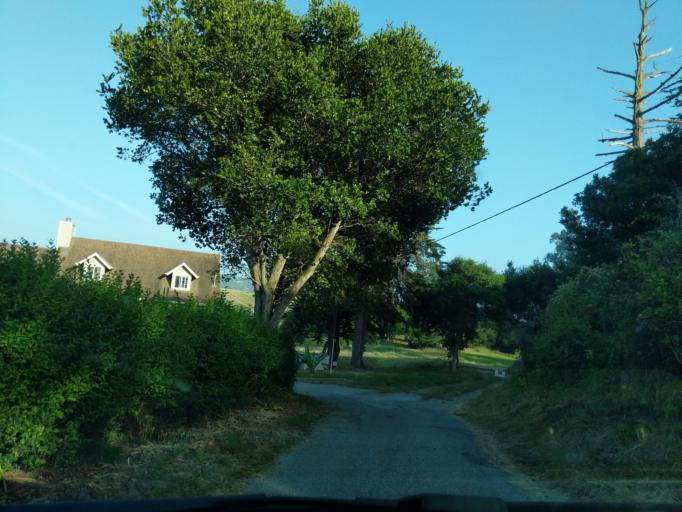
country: US
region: California
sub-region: Monterey County
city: Las Lomas
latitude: 36.8658
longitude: -121.7600
